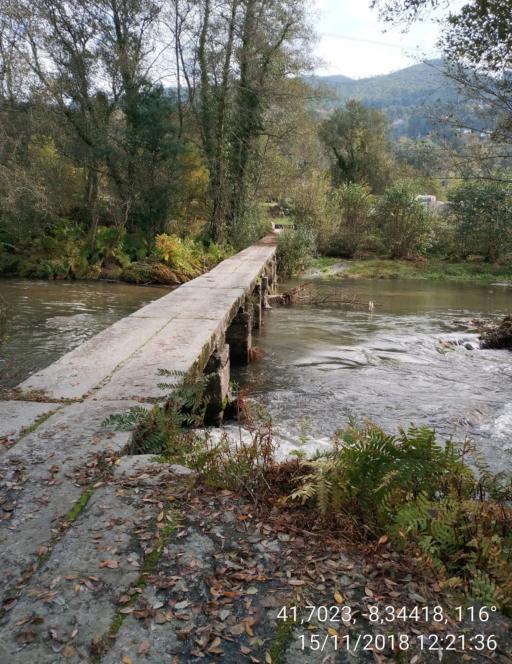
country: PT
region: Braga
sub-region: Terras de Bouro
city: Terras de Bouro
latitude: 41.7018
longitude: -8.3380
